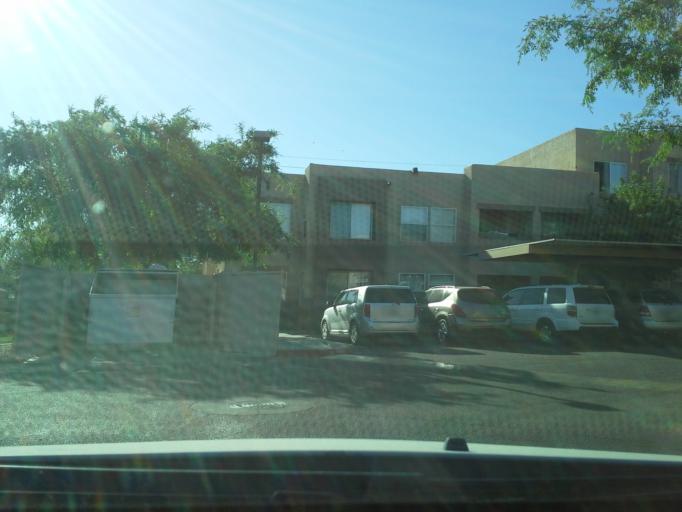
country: US
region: Arizona
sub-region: Maricopa County
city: Glendale
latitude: 33.5364
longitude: -112.2110
